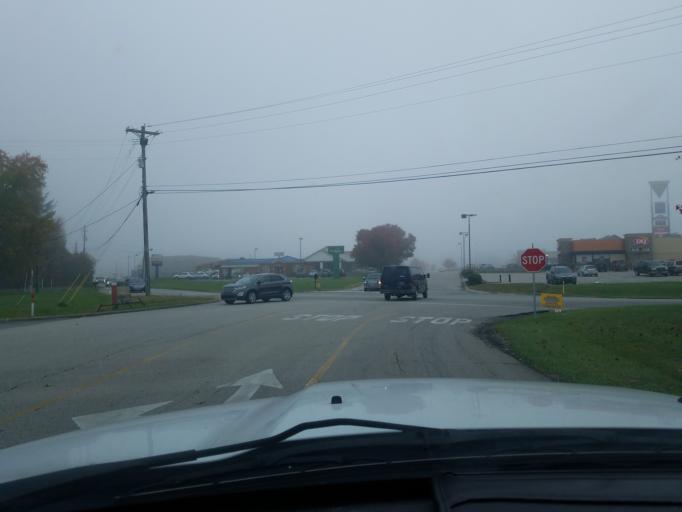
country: US
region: Indiana
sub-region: Floyd County
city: Galena
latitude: 38.3139
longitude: -85.8987
